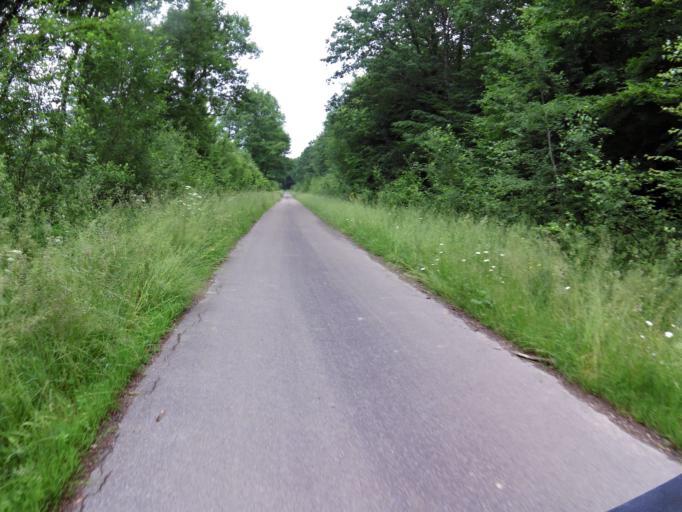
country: FR
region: Champagne-Ardenne
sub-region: Departement de la Haute-Marne
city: Montier-en-Der
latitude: 48.5472
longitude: 4.8188
